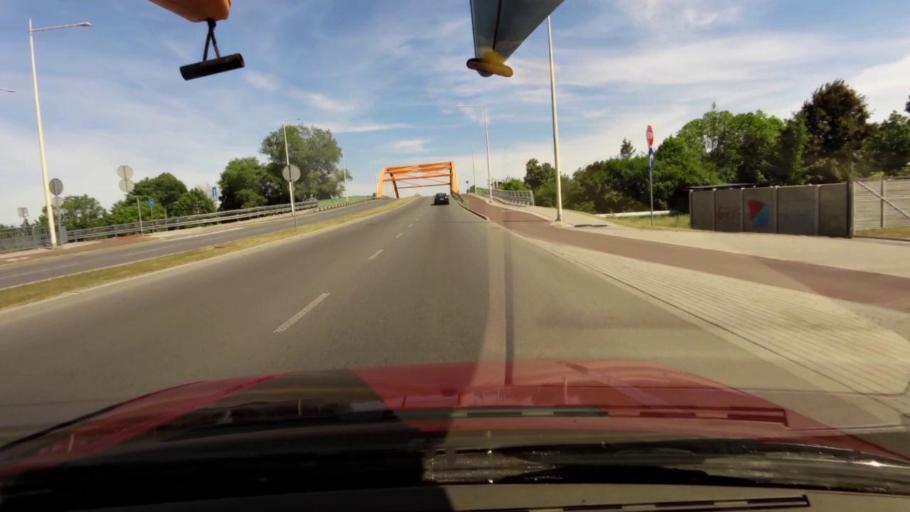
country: PL
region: Pomeranian Voivodeship
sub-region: Powiat slupski
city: Kobylnica
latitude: 54.4553
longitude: 17.0085
